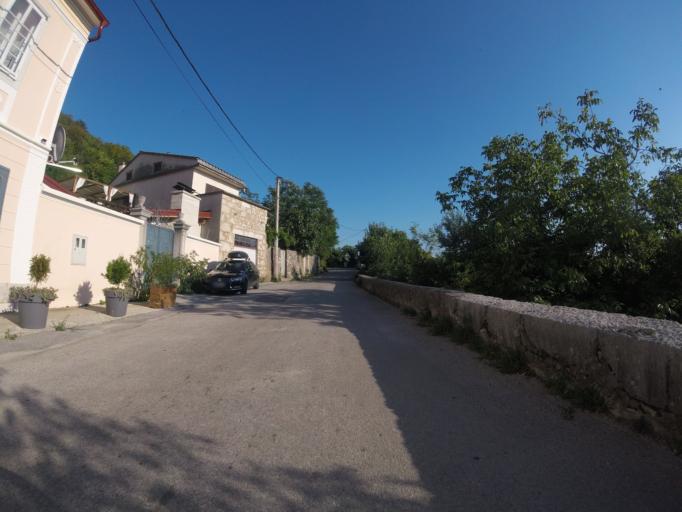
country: HR
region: Primorsko-Goranska
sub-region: Grad Crikvenica
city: Crikvenica
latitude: 45.1969
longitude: 14.7212
